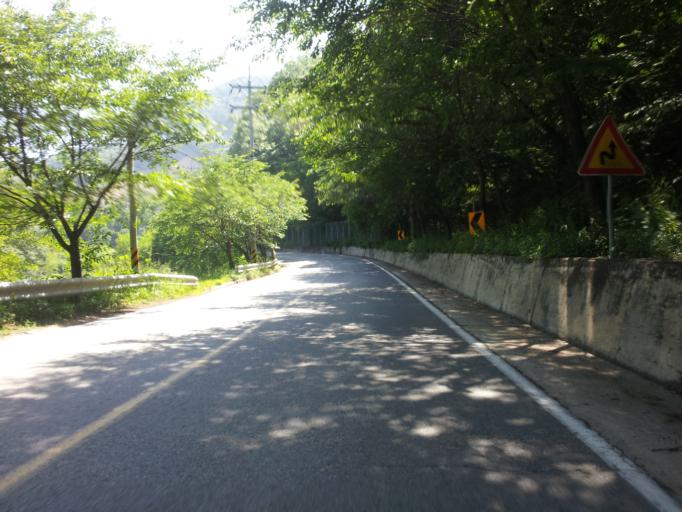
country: KR
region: Chungcheongbuk-do
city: Okcheon
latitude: 36.4534
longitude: 127.6802
